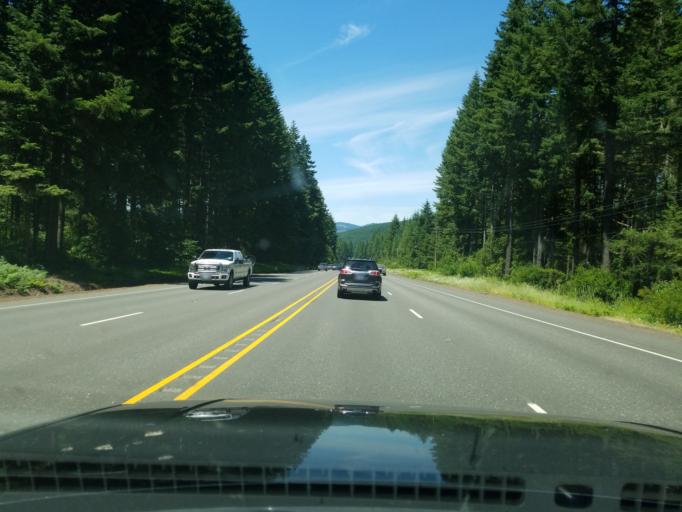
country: US
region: Oregon
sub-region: Columbia County
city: Vernonia
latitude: 45.7542
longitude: -123.2816
